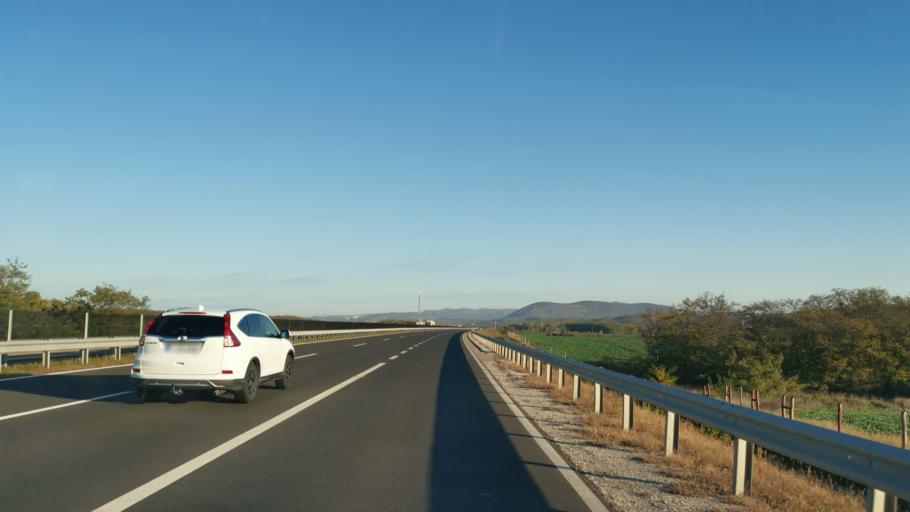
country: HU
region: Heves
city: Andornaktalya
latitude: 47.8421
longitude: 20.3988
